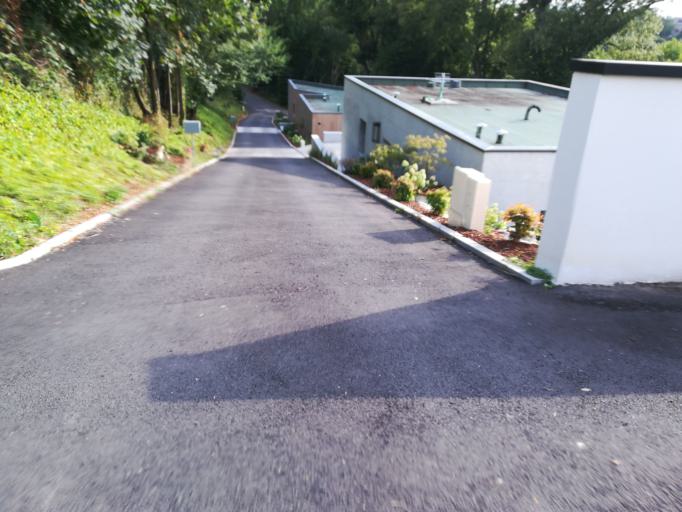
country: FR
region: Haute-Normandie
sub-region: Departement de la Seine-Maritime
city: Mont-Saint-Aignan
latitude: 49.4634
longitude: 1.0913
